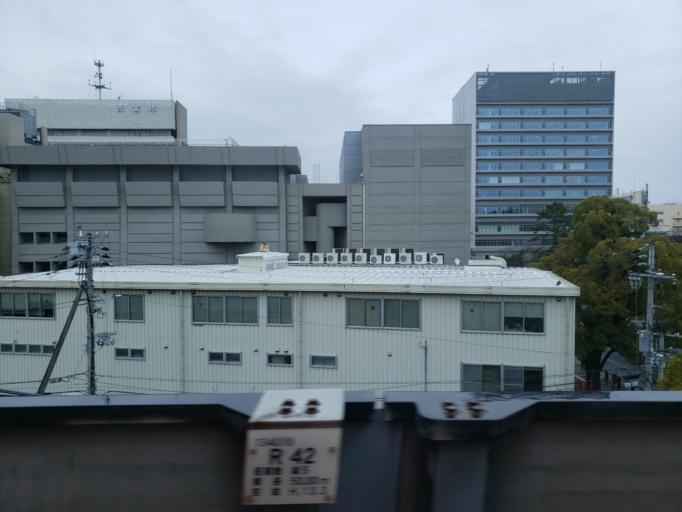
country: JP
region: Hyogo
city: Nishinomiya-hama
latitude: 34.7365
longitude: 135.3416
